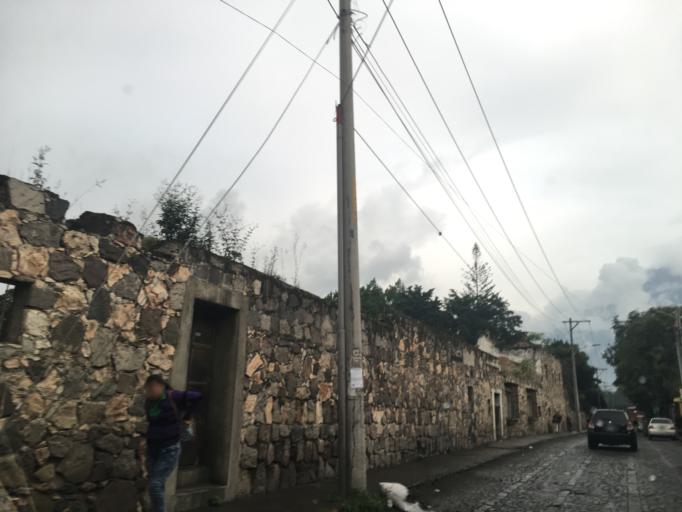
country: GT
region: Sacatepequez
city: Antigua Guatemala
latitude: 14.5561
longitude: -90.7401
